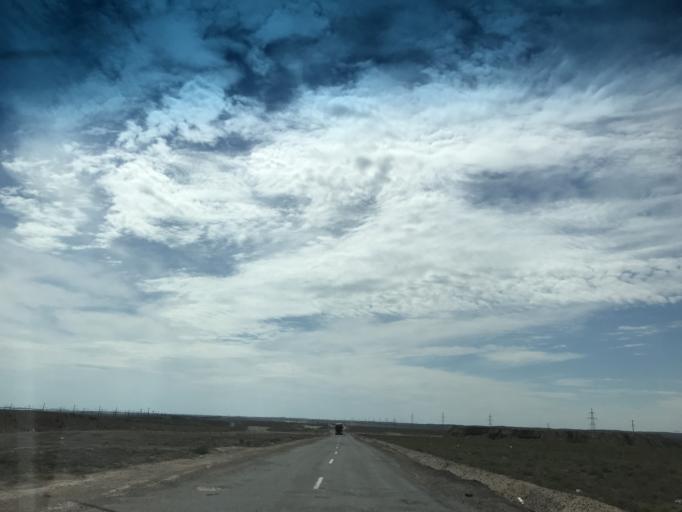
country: KZ
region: Almaty Oblysy
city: Ulken
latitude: 45.2619
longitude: 73.7986
